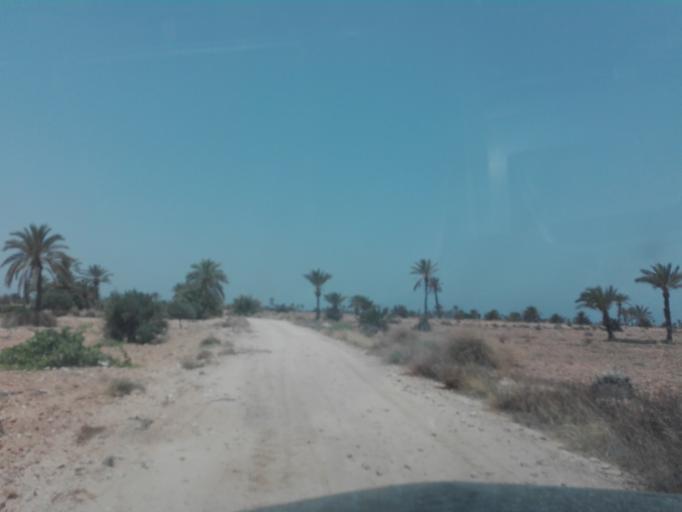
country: TN
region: Safaqis
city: Al Qarmadah
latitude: 34.6586
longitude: 11.1011
